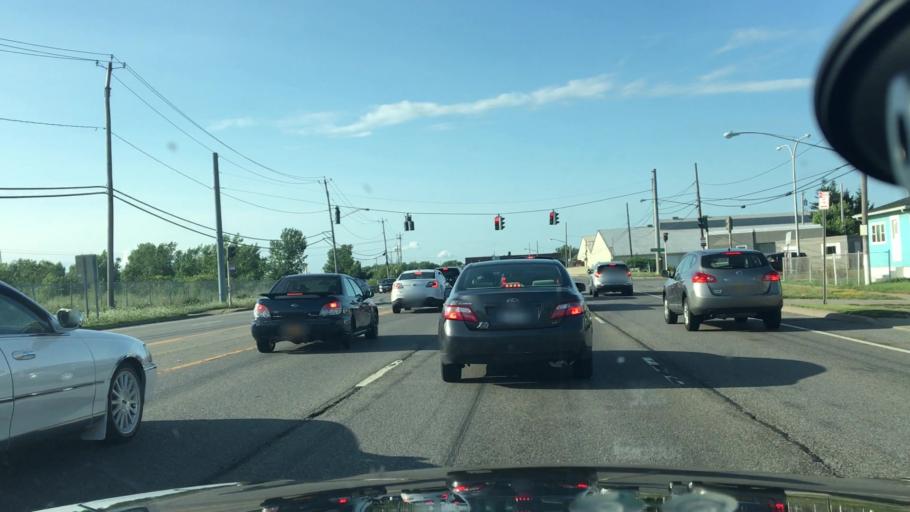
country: US
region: New York
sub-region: Erie County
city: Lackawanna
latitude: 42.8118
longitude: -78.8454
